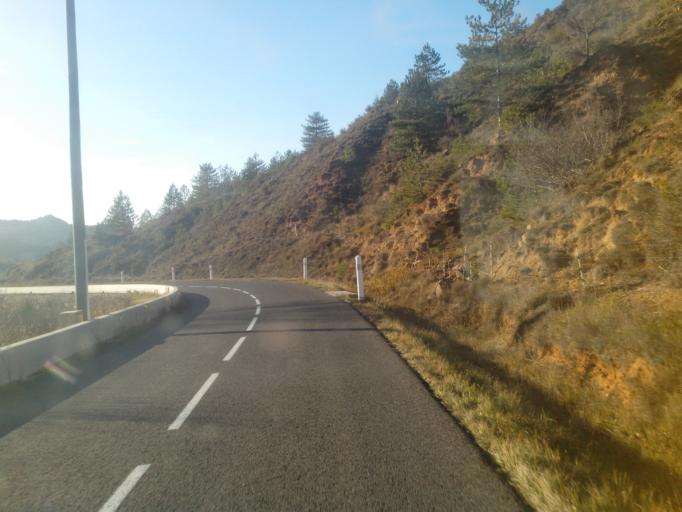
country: FR
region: Languedoc-Roussillon
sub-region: Departement de l'Aude
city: Couiza
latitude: 42.9398
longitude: 2.2910
